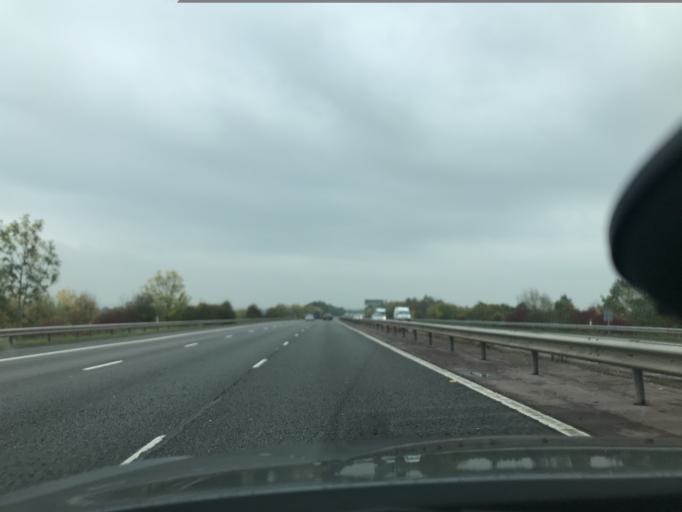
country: GB
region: England
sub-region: Oxfordshire
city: Bicester
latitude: 51.8601
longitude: -1.1847
